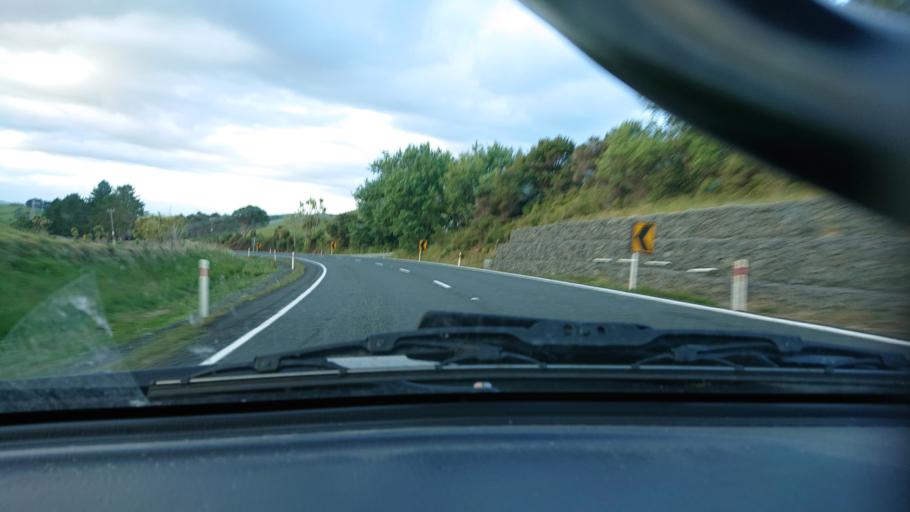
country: NZ
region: Auckland
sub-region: Auckland
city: Parakai
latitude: -36.4720
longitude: 174.4498
